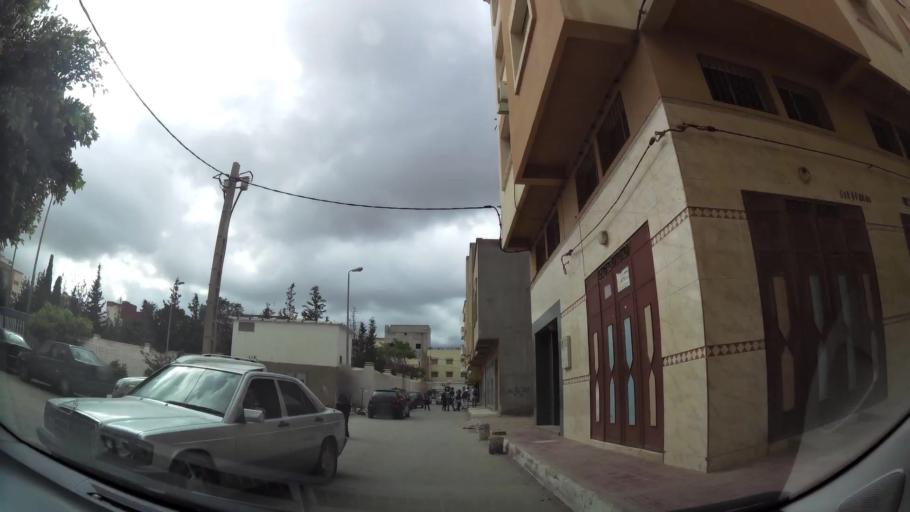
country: MA
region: Oriental
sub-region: Nador
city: Nador
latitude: 35.1703
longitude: -2.9371
